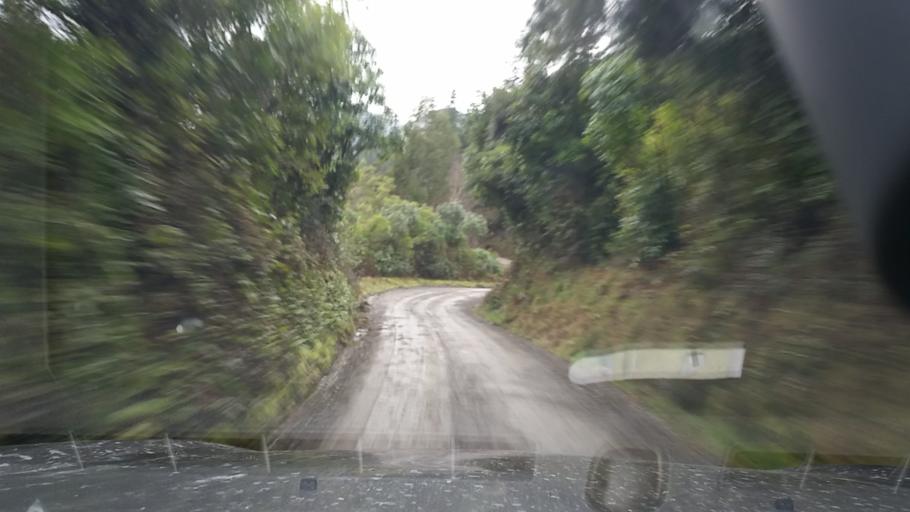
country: NZ
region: Nelson
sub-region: Nelson City
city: Nelson
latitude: -41.3603
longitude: 173.6165
